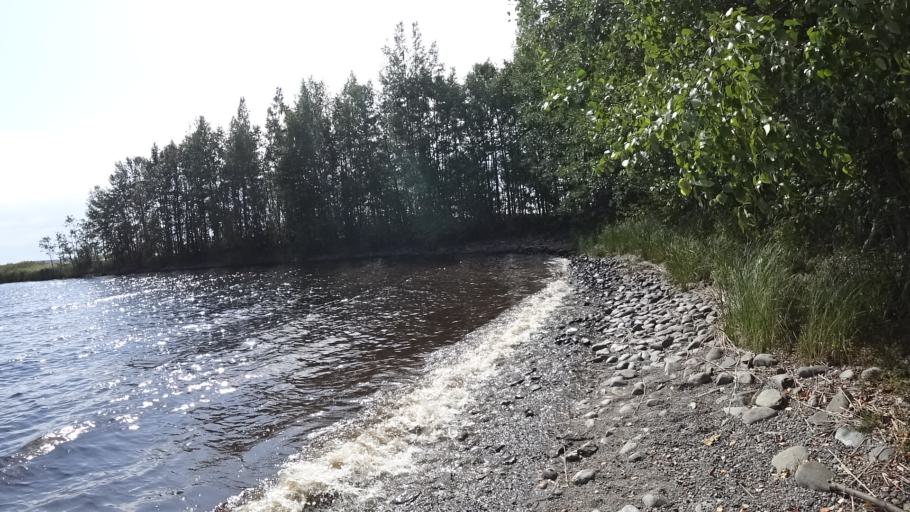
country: FI
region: North Karelia
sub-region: Keski-Karjala
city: Raeaekkylae
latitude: 62.3946
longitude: 29.7594
